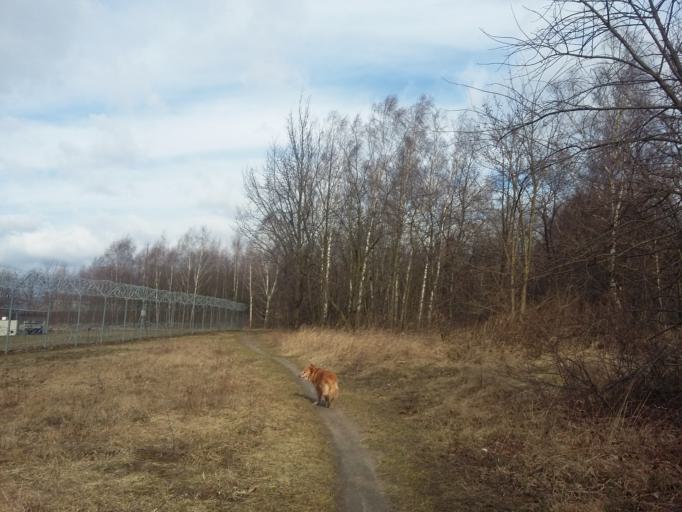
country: PL
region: Lodz Voivodeship
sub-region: Powiat pabianicki
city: Ksawerow
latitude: 51.7259
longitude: 19.4074
